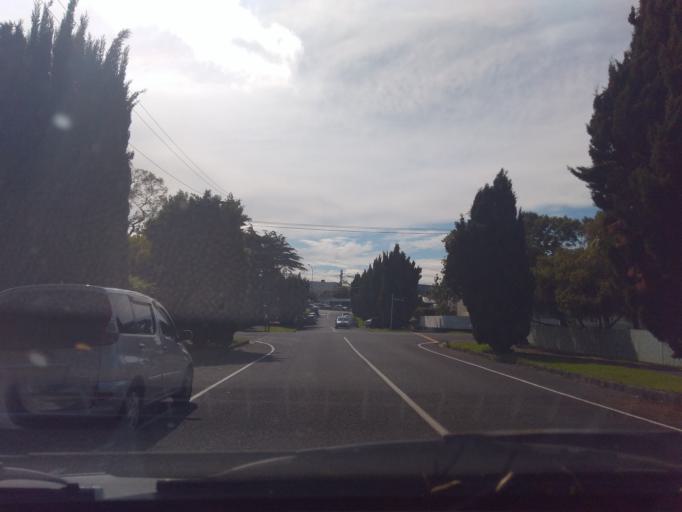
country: NZ
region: Auckland
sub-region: Auckland
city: Auckland
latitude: -36.8754
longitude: 174.7306
